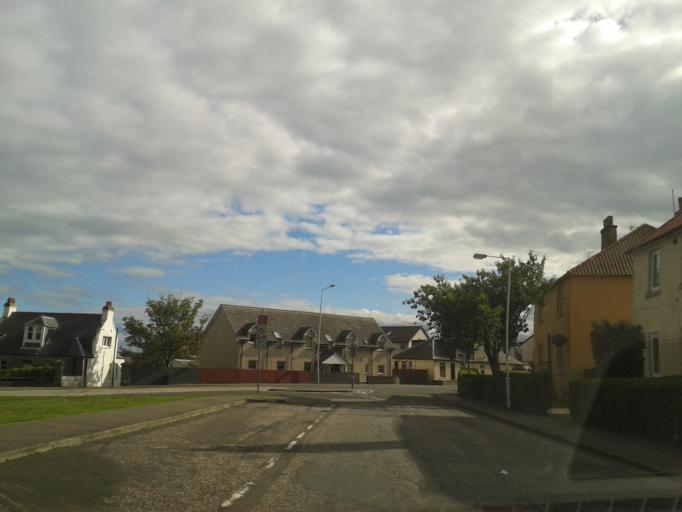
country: GB
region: Scotland
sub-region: Fife
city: Kirkcaldy
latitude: 56.0958
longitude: -3.1656
